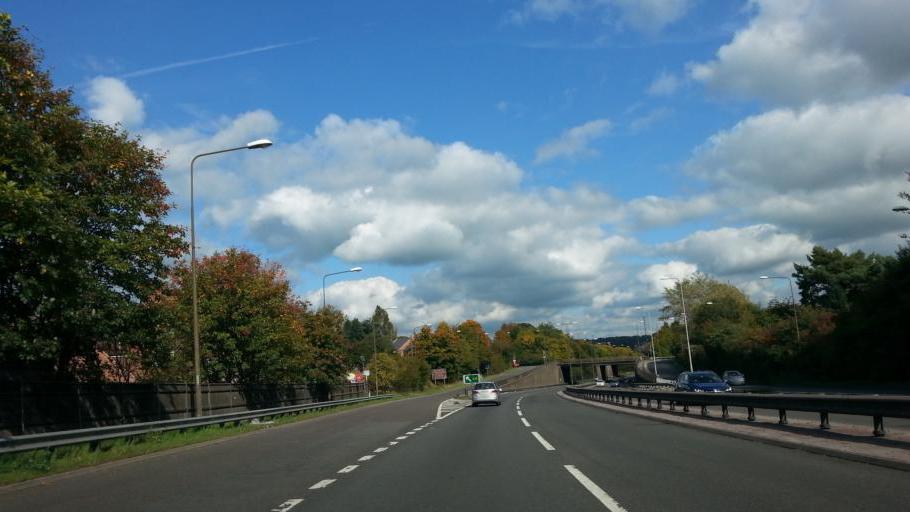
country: GB
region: England
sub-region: Derby
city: Derby
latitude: 52.9487
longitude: -1.4836
